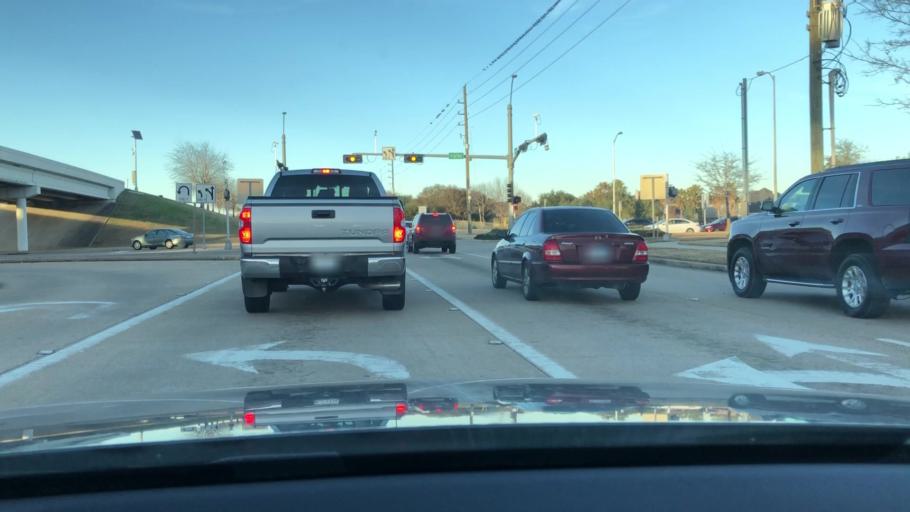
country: US
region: Texas
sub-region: Fort Bend County
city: Cinco Ranch
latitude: 29.7136
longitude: -95.7730
